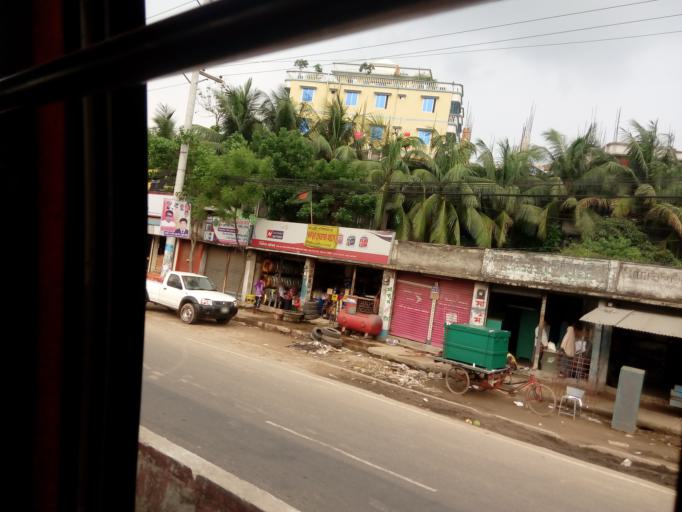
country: BD
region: Dhaka
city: Tungi
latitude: 23.9431
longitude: 90.2720
